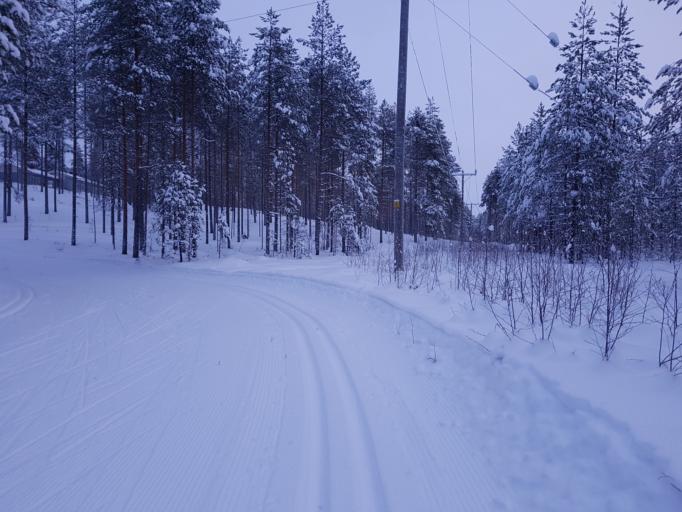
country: FI
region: Kainuu
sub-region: Kehys-Kainuu
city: Kuhmo
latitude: 64.1172
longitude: 29.5747
